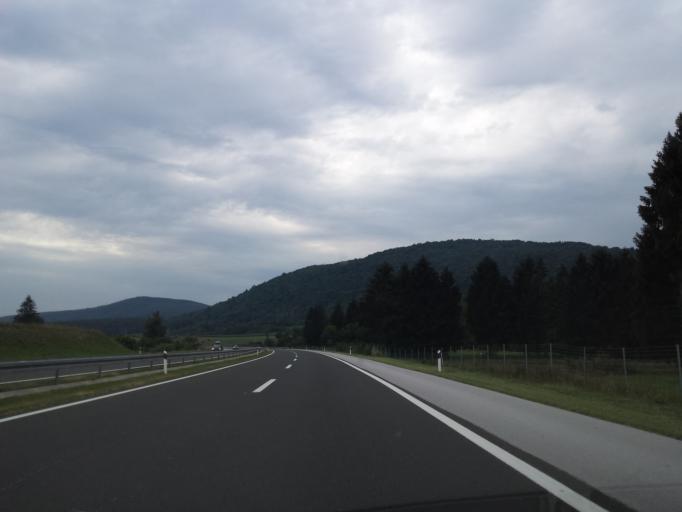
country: HR
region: Karlovacka
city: Ostarije
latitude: 45.2193
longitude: 15.2590
